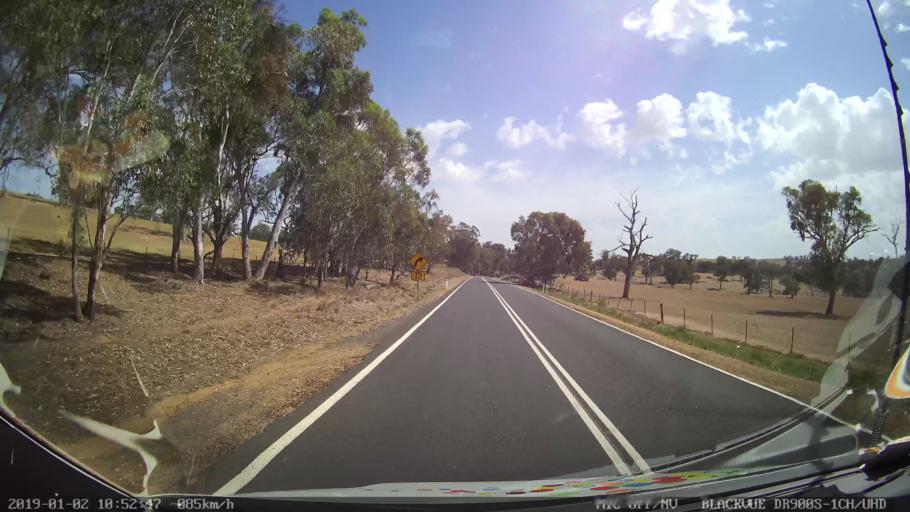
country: AU
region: New South Wales
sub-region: Cootamundra
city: Cootamundra
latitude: -34.6849
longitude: 148.2714
